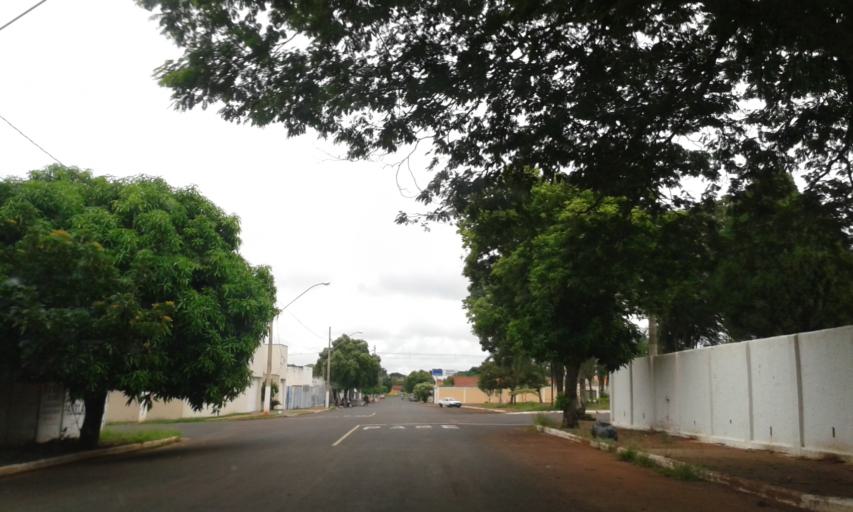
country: BR
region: Minas Gerais
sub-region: Ituiutaba
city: Ituiutaba
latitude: -18.9668
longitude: -49.4548
